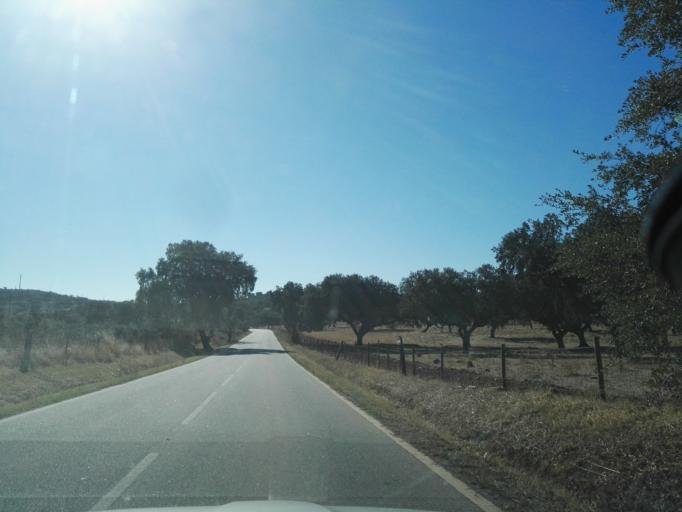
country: PT
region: Portalegre
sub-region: Elvas
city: Elvas
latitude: 38.9147
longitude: -7.1821
